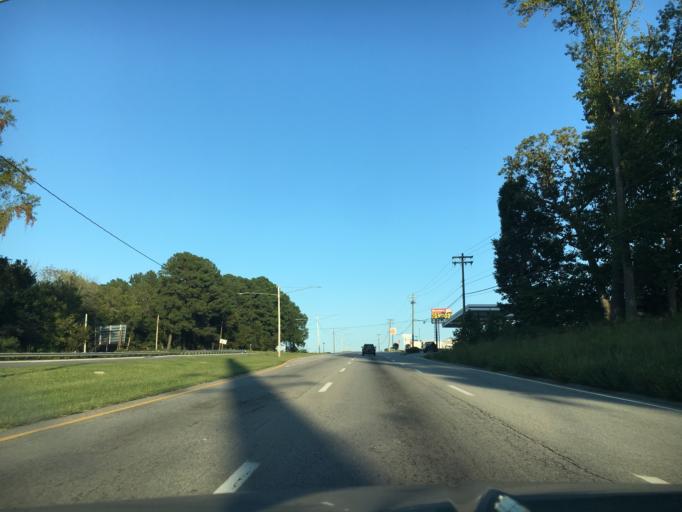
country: US
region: Virginia
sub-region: City of Danville
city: Danville
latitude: 36.5820
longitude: -79.3502
